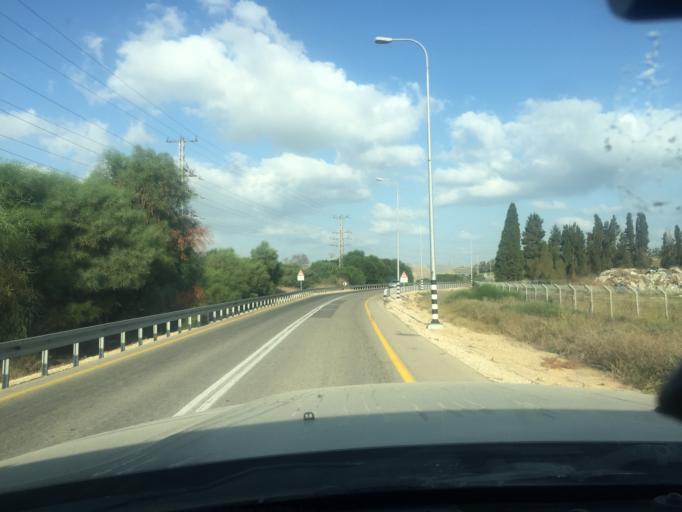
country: PS
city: Umm an Nasr
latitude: 31.6092
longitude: 34.5357
